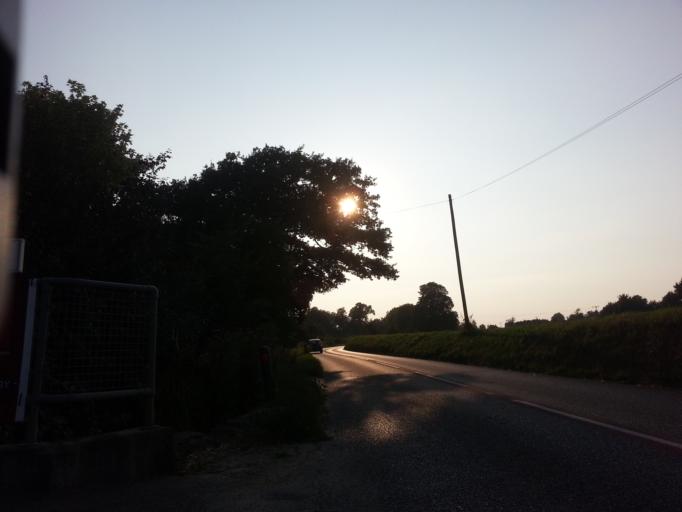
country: GB
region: England
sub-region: Suffolk
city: Bramford
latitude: 52.0951
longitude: 1.0562
